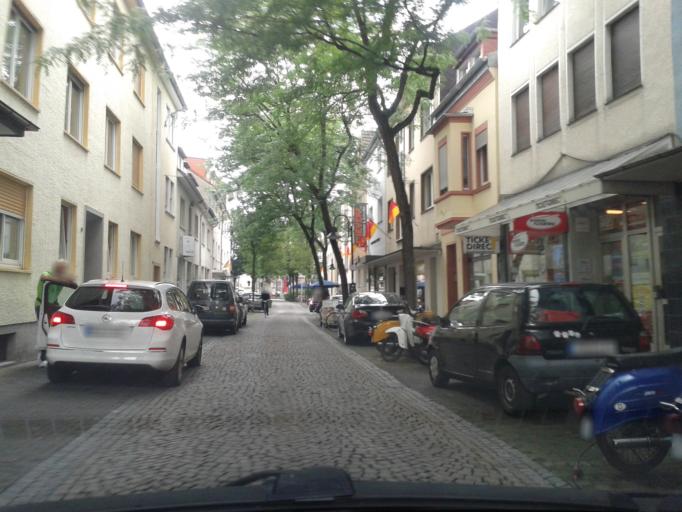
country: DE
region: North Rhine-Westphalia
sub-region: Regierungsbezirk Detmold
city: Paderborn
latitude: 51.7196
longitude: 8.7492
